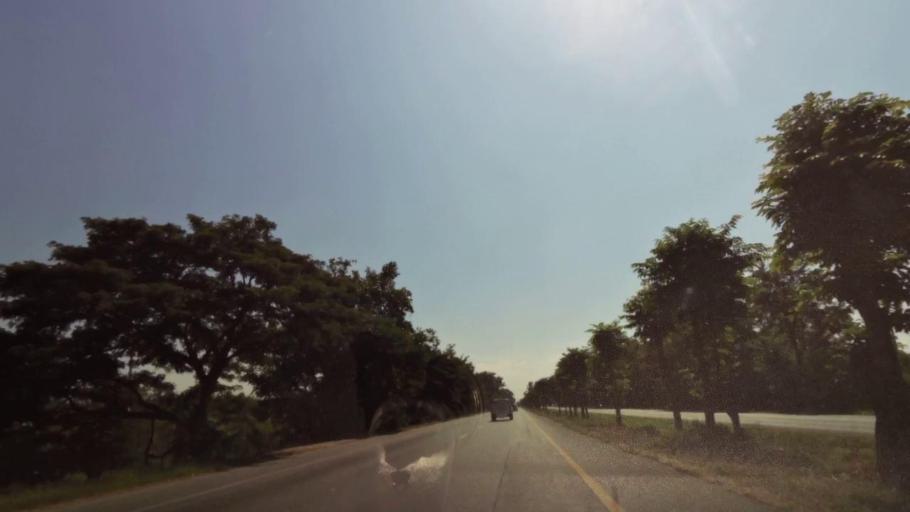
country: TH
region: Nakhon Sawan
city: Kao Liao
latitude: 15.7918
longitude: 100.1208
